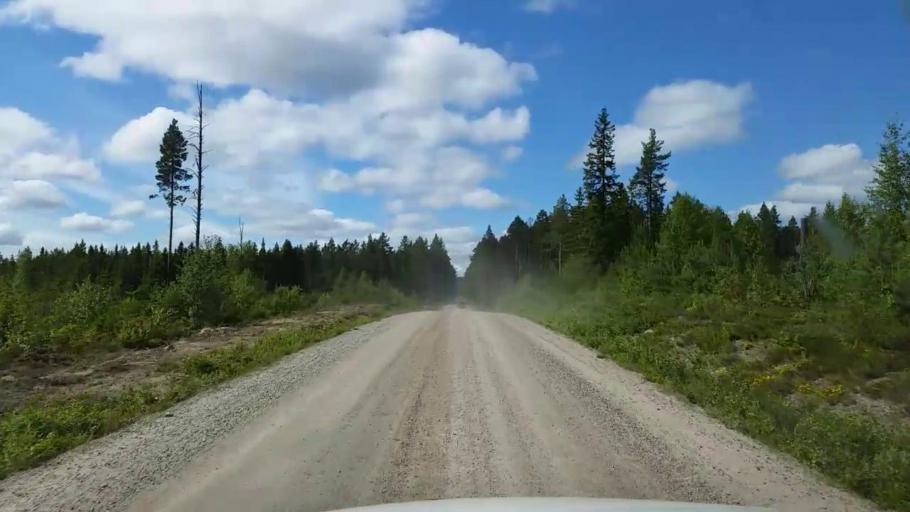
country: SE
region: Gaevleborg
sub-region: Ovanakers Kommun
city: Edsbyn
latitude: 61.5735
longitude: 15.9158
